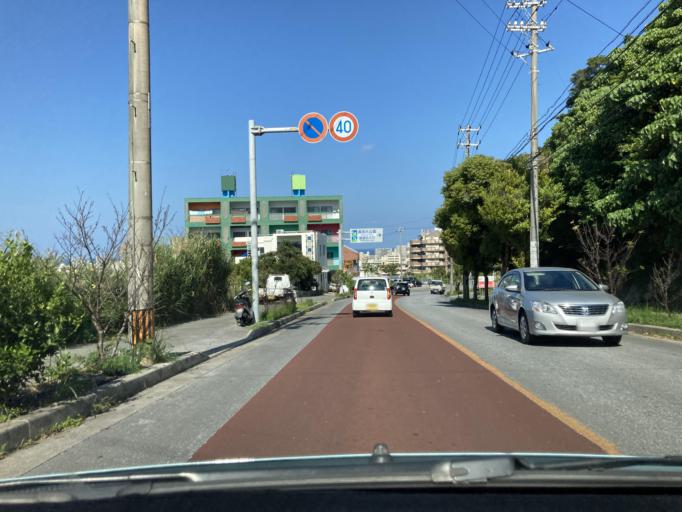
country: JP
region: Okinawa
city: Ginowan
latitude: 26.2529
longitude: 127.7251
